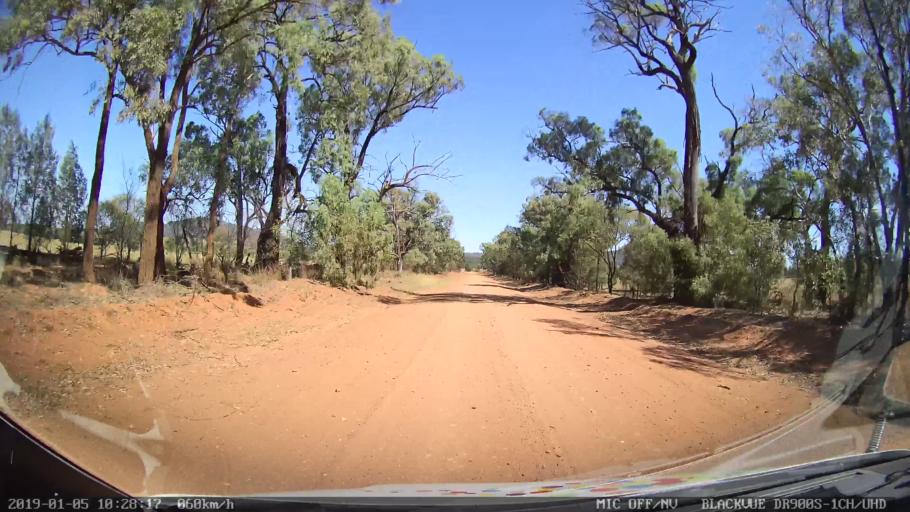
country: AU
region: New South Wales
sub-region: Gilgandra
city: Gilgandra
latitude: -31.5461
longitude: 148.9398
